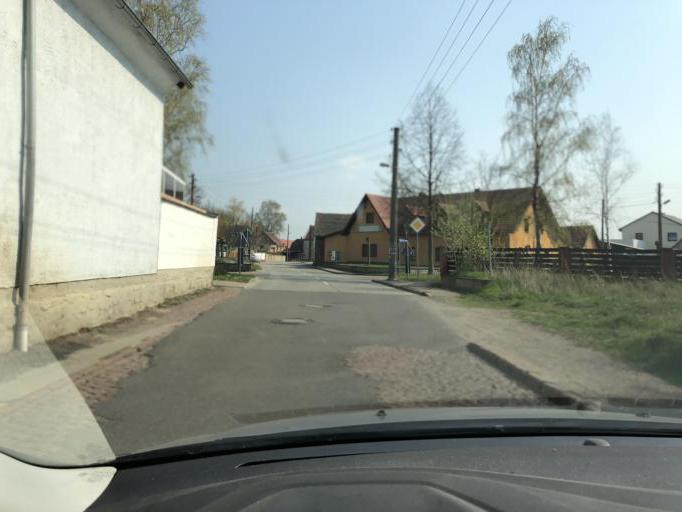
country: DE
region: Saxony-Anhalt
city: Hohenthurm
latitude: 51.5004
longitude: 12.0978
